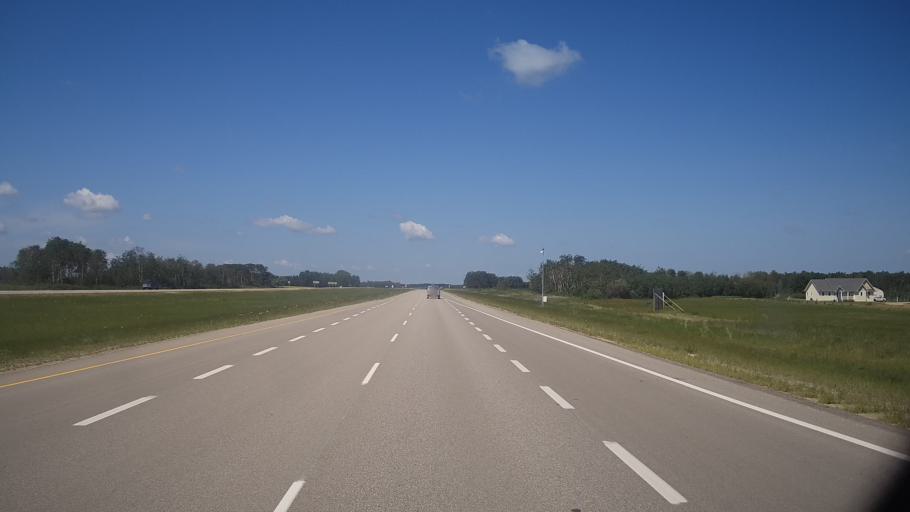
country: CA
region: Saskatchewan
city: Saskatoon
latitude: 52.0123
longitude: -106.3926
